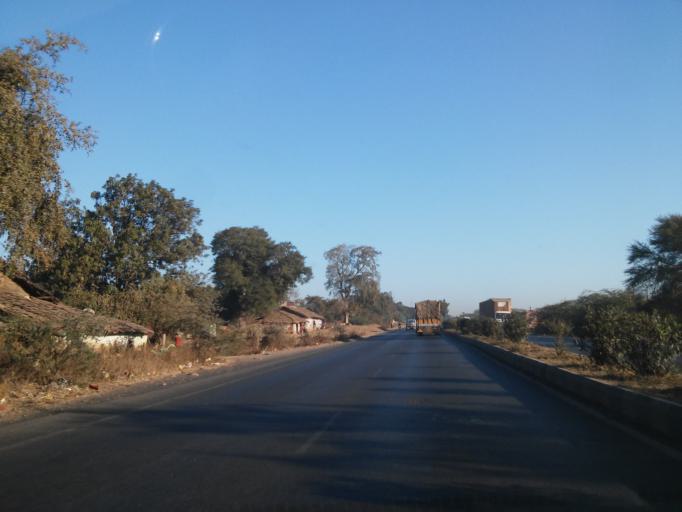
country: IN
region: Rajasthan
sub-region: Dungarpur
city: Dungarpur
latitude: 23.8713
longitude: 73.5285
